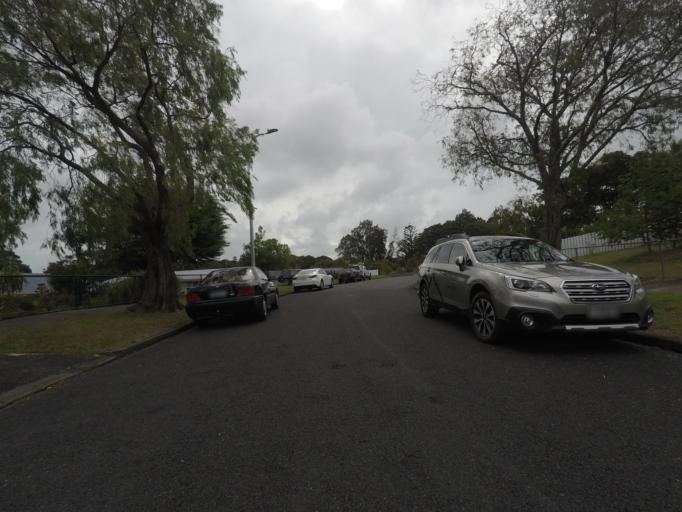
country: NZ
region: Auckland
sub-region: Auckland
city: Rosebank
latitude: -36.8854
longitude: 174.6752
